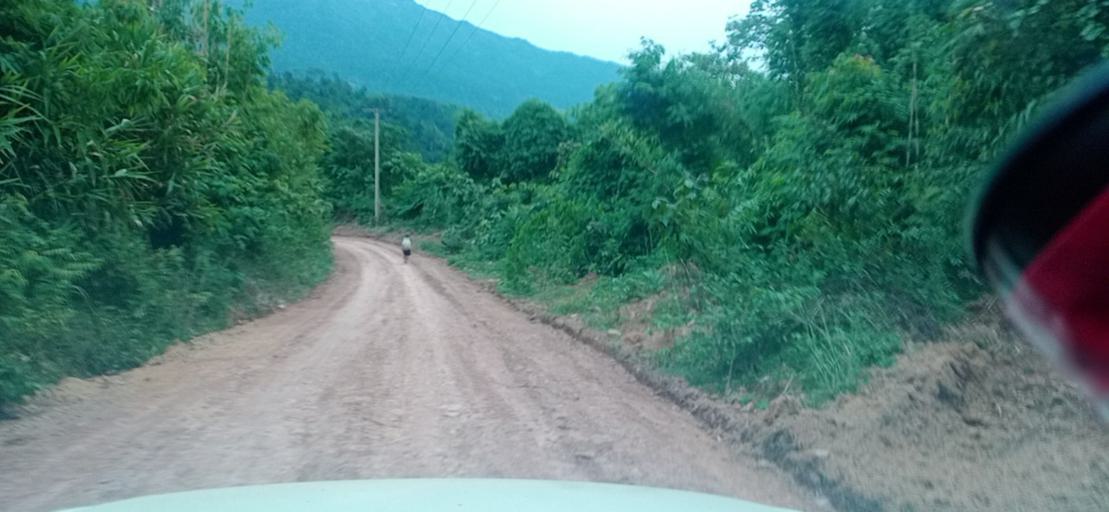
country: TH
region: Changwat Bueng Kan
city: Pak Khat
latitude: 18.5517
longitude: 103.4276
